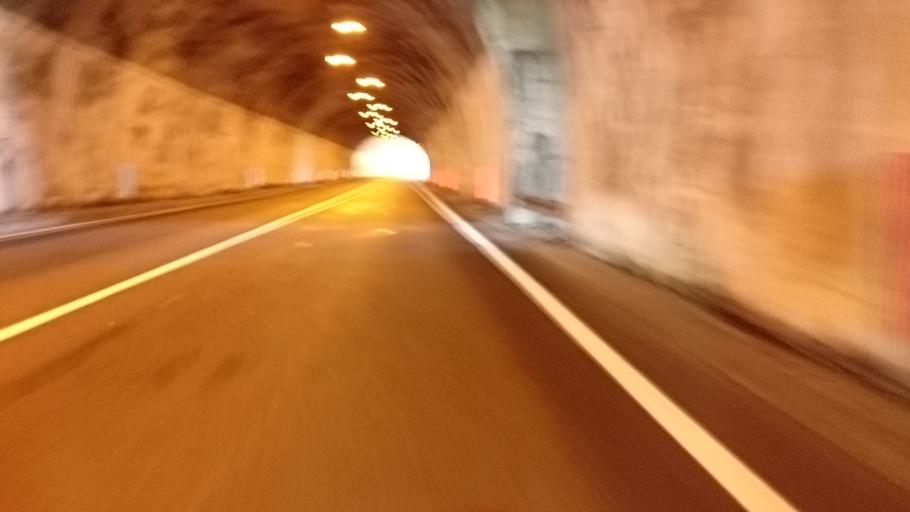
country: IT
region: Veneto
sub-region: Provincia di Belluno
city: Farra d'Alpago
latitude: 46.0917
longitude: 12.3408
